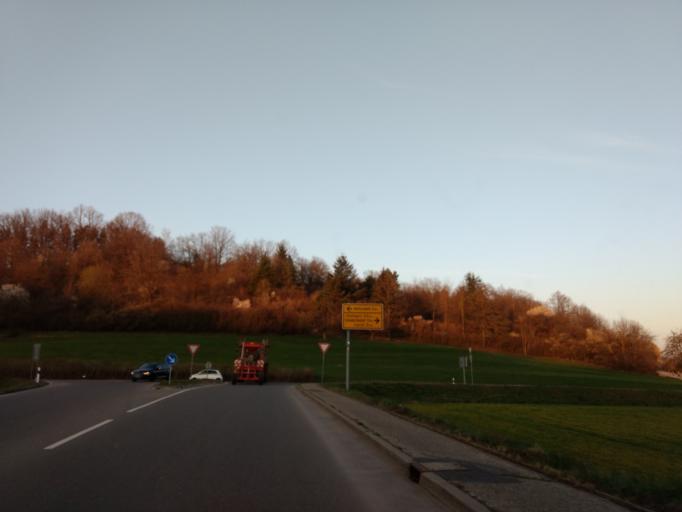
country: DE
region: Baden-Wuerttemberg
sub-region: Regierungsbezirk Stuttgart
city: Lorch
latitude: 48.7998
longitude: 9.6647
